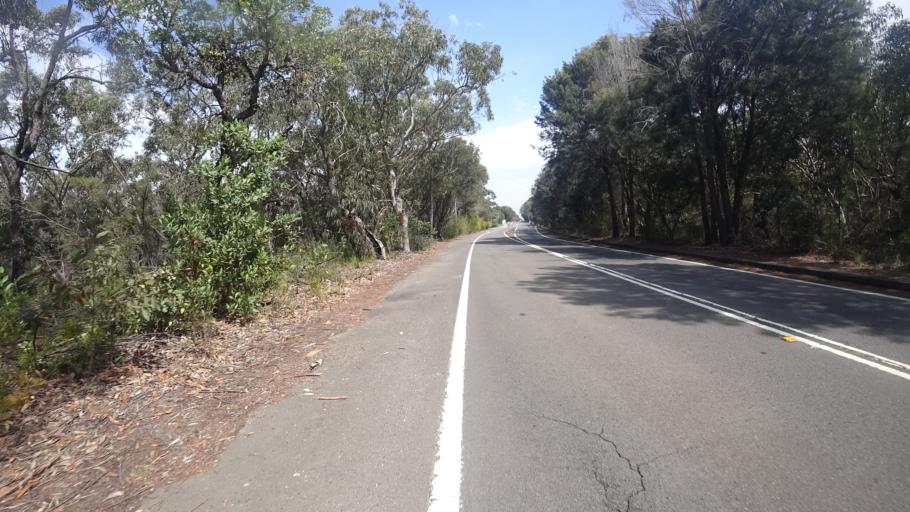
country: AU
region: New South Wales
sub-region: Hornsby Shire
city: Mount Colah
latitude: -33.6790
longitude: 151.1228
